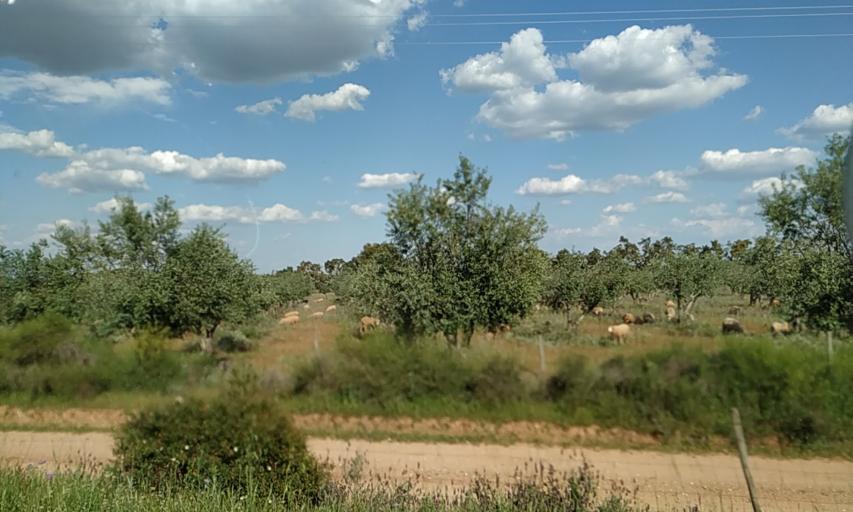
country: PT
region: Evora
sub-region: Estremoz
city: Estremoz
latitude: 38.8862
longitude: -7.5573
